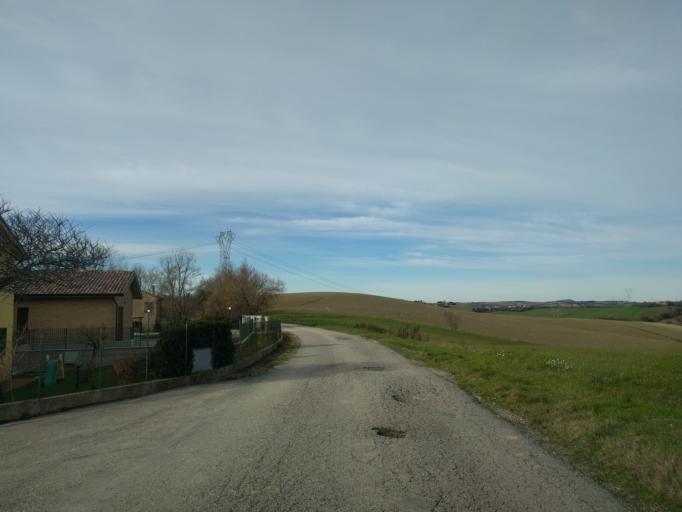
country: IT
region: The Marches
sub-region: Provincia di Pesaro e Urbino
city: Cuccurano
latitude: 43.8108
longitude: 12.9348
